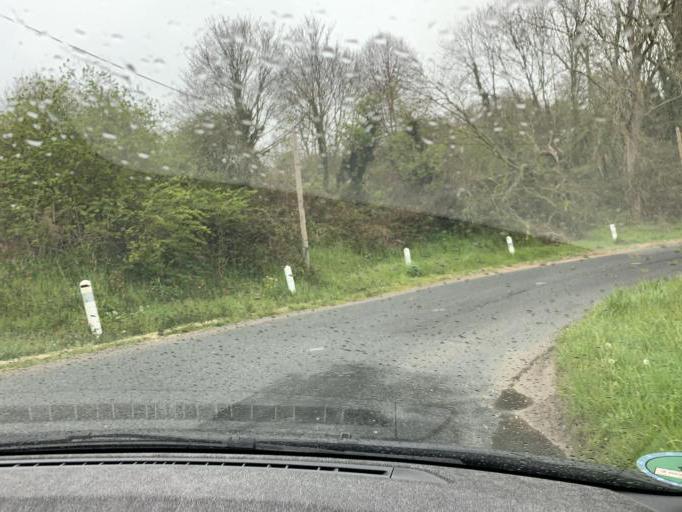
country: FR
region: Haute-Normandie
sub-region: Departement de la Seine-Maritime
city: Etretat
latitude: 49.7121
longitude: 0.2243
